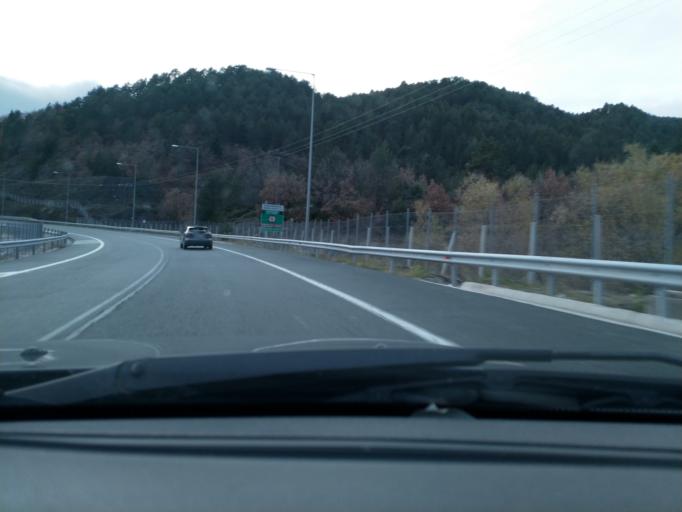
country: GR
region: Epirus
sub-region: Nomos Ioanninon
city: Metsovo
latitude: 39.7947
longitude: 21.3027
